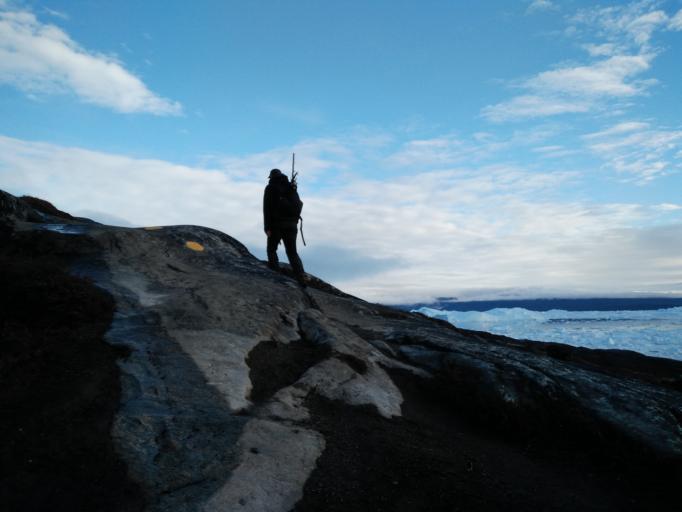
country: GL
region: Qaasuitsup
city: Ilulissat
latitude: 69.2053
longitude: -51.1286
